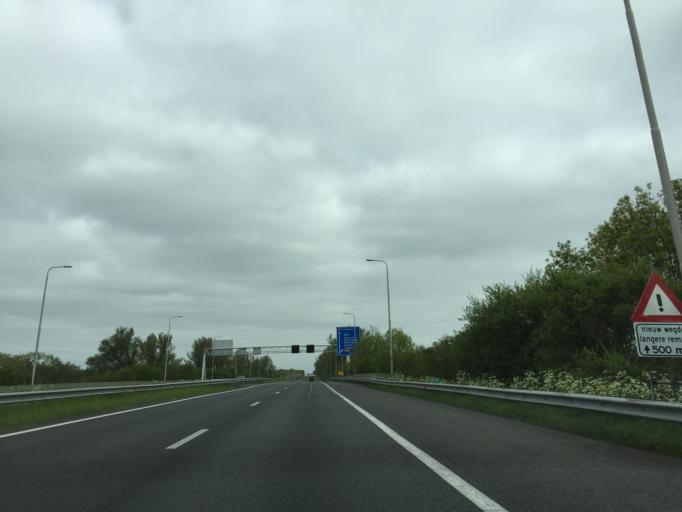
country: NL
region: North Holland
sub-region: Gemeente Hoorn
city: Hoorn
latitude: 52.6804
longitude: 5.0307
